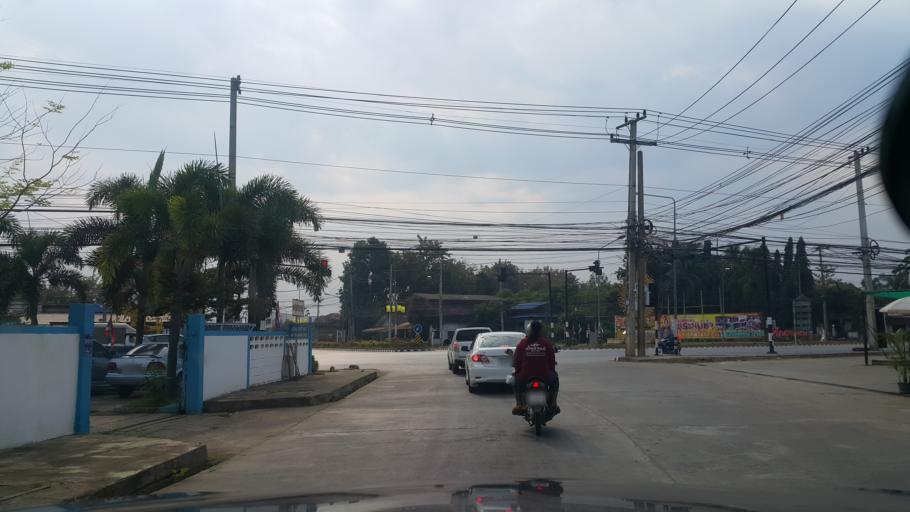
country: TH
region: Sukhothai
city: Si Samrong
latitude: 17.1634
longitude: 99.8615
